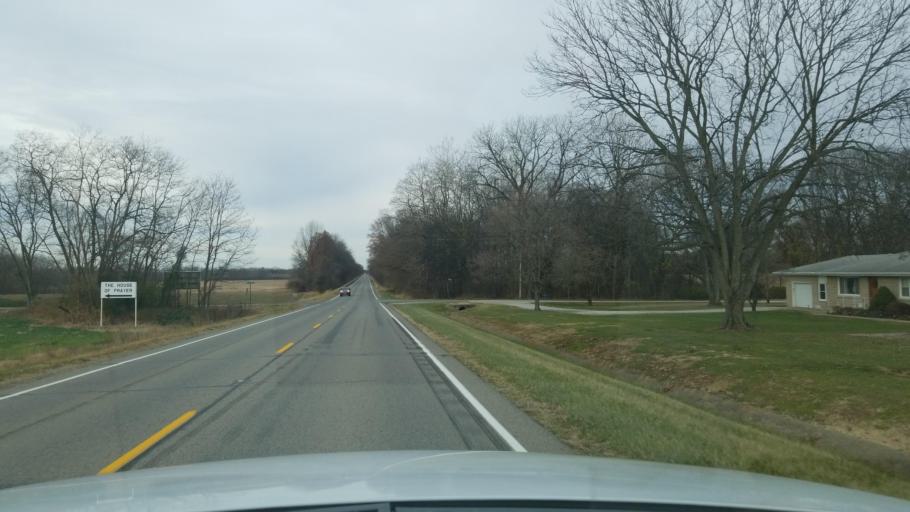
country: US
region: Indiana
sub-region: Posey County
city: Mount Vernon
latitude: 37.9291
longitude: -87.9620
